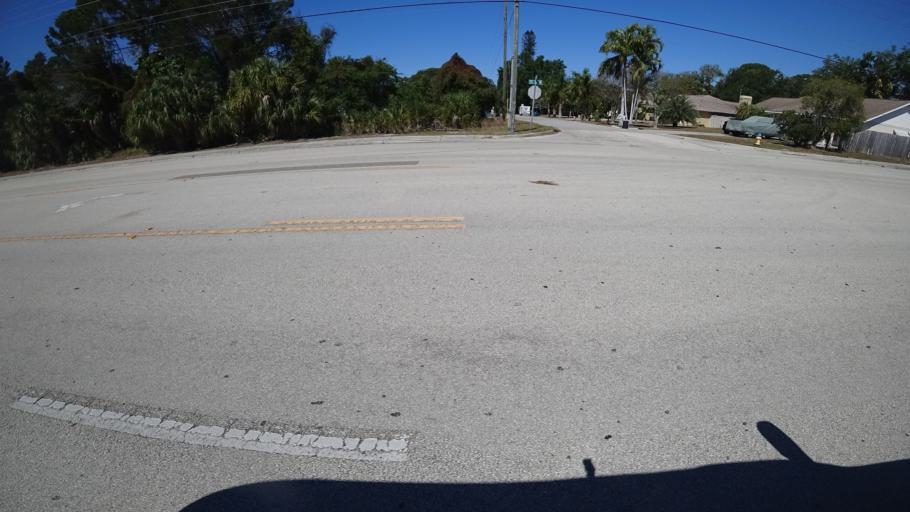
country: US
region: Florida
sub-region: Manatee County
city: West Bradenton
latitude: 27.4770
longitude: -82.6368
